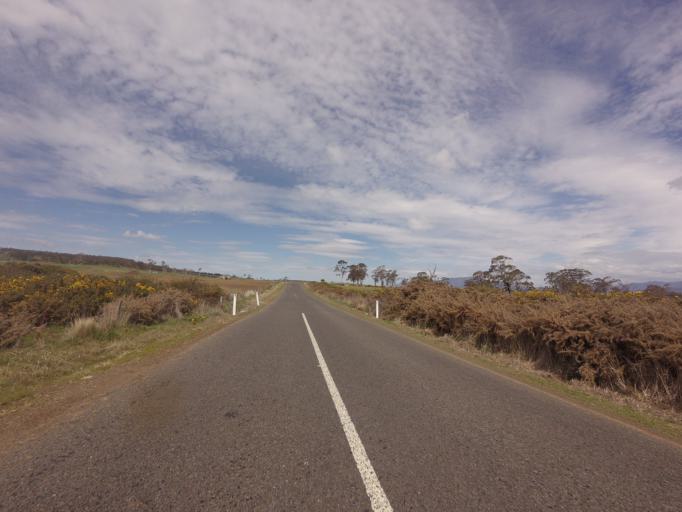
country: AU
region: Tasmania
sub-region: Northern Midlands
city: Longford
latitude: -41.7391
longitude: 147.2018
